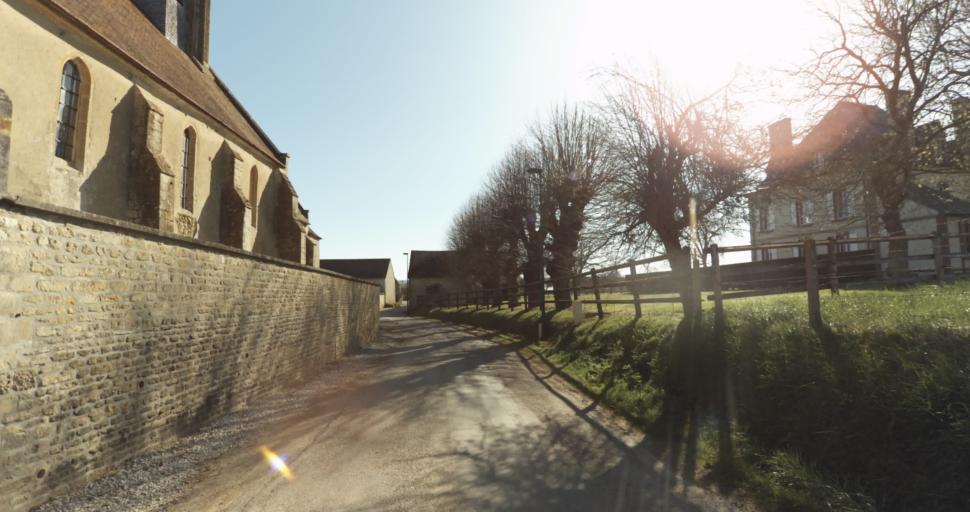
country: FR
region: Lower Normandy
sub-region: Departement du Calvados
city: Saint-Pierre-sur-Dives
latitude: 48.9891
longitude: -0.0201
